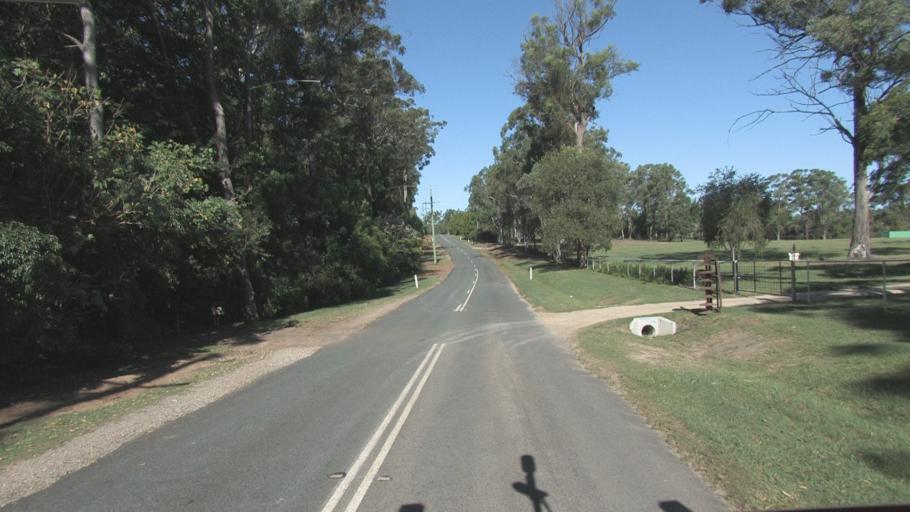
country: AU
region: Queensland
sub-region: Logan
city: Springwood
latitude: -27.5930
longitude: 153.1571
